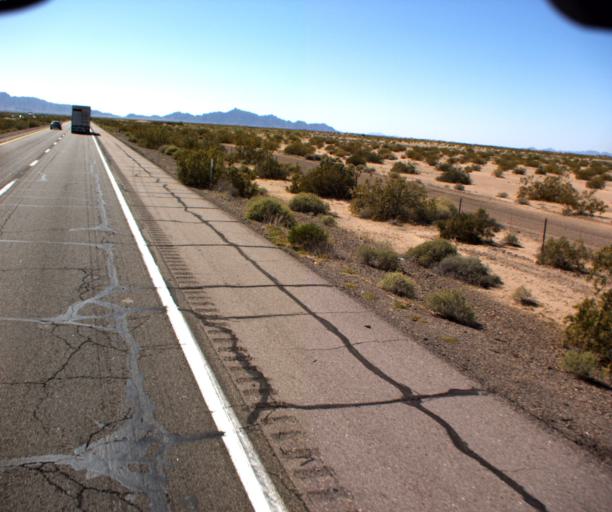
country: US
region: Arizona
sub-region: Yuma County
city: Wellton
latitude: 32.7798
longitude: -113.5858
